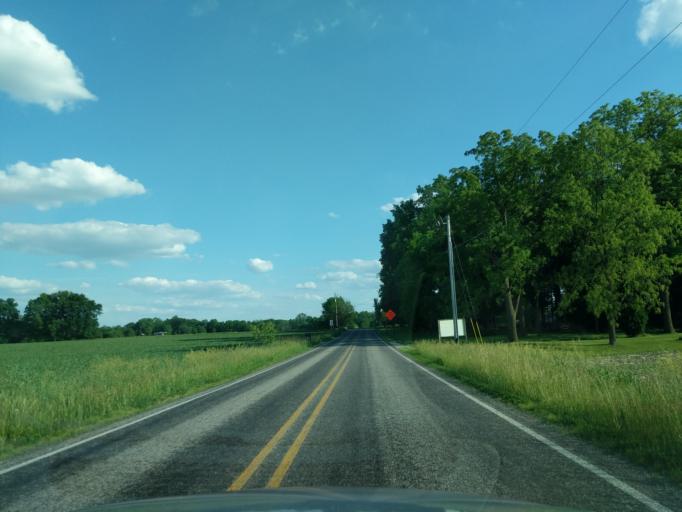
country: US
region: Indiana
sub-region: Kosciusko County
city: North Webster
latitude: 41.3043
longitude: -85.6434
